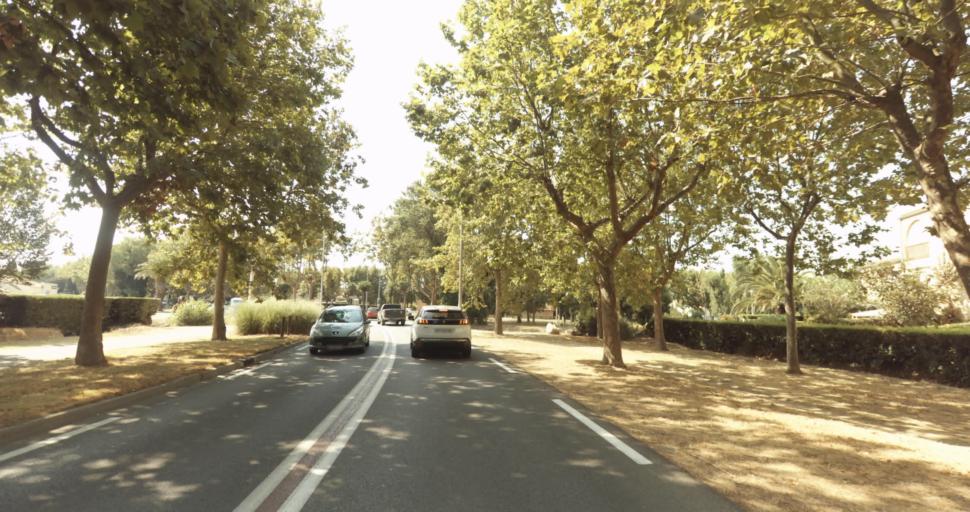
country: FR
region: Languedoc-Roussillon
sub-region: Departement des Pyrenees-Orientales
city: Saint-Cyprien-Plage
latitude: 42.6102
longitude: 3.0285
